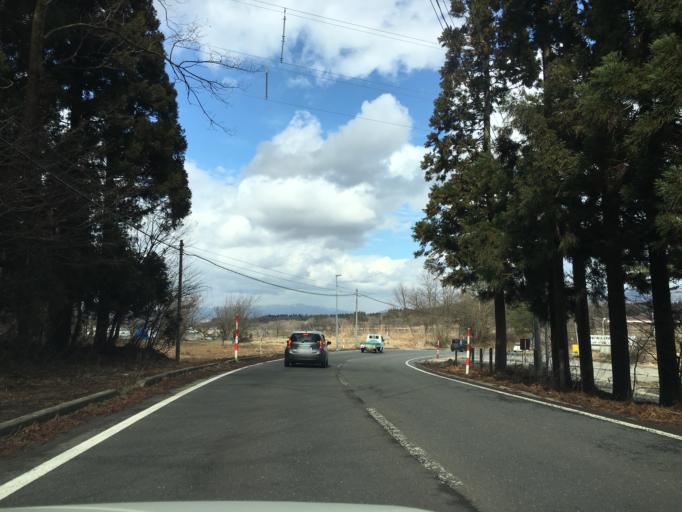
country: JP
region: Akita
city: Odate
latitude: 40.2032
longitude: 140.5554
